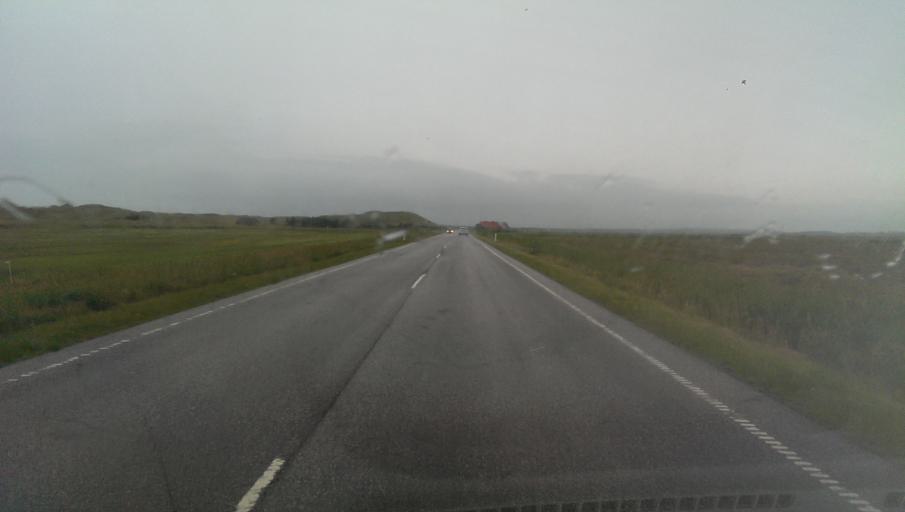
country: DK
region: Central Jutland
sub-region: Ringkobing-Skjern Kommune
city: Ringkobing
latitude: 56.2265
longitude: 8.1398
